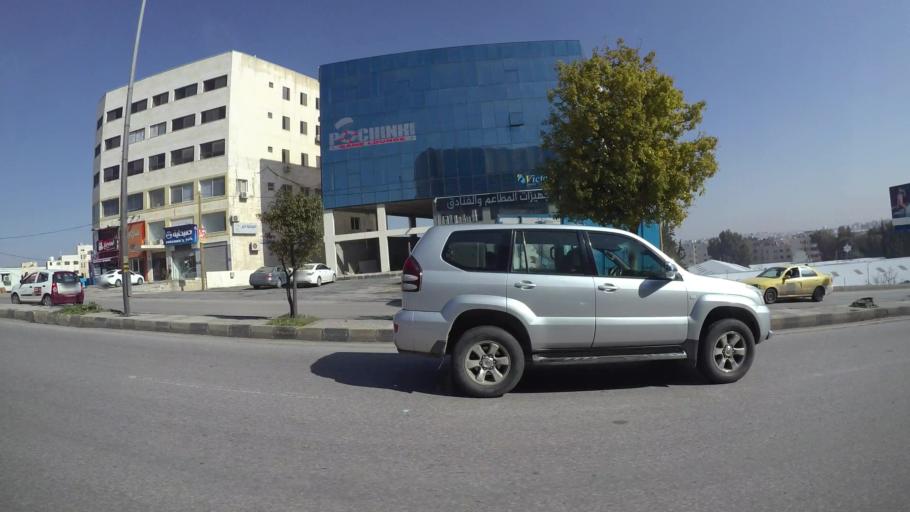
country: JO
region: Amman
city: Al Bunayyat ash Shamaliyah
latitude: 31.9182
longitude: 35.8994
